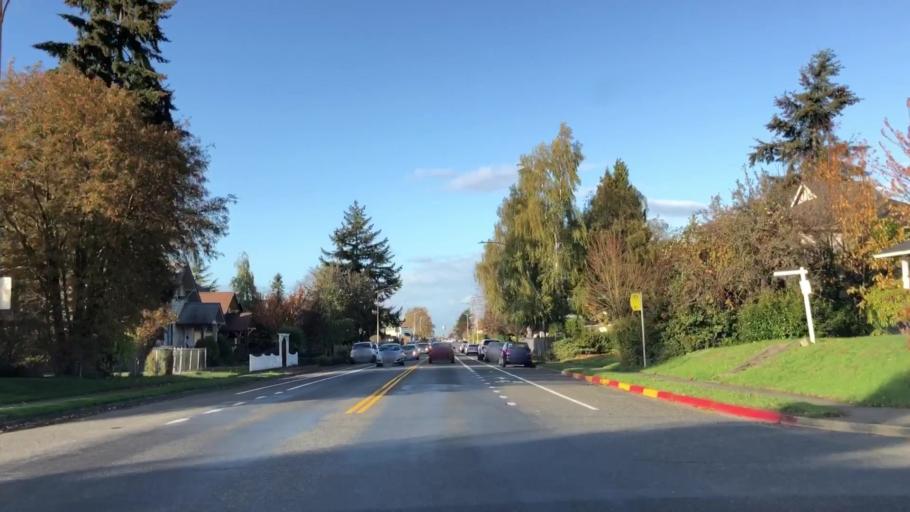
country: US
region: Washington
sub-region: Pierce County
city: Tacoma
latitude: 47.2037
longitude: -122.4432
